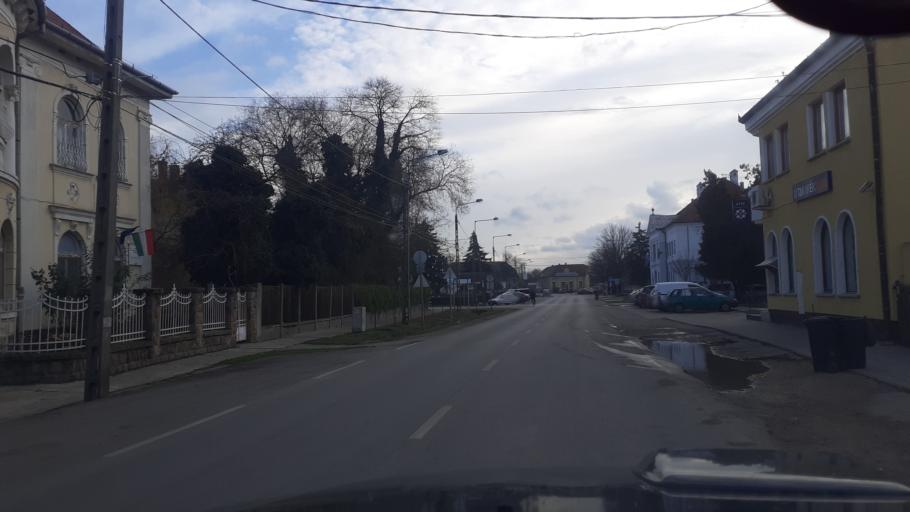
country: HU
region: Bacs-Kiskun
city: Szabadszallas
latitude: 46.8768
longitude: 19.2215
